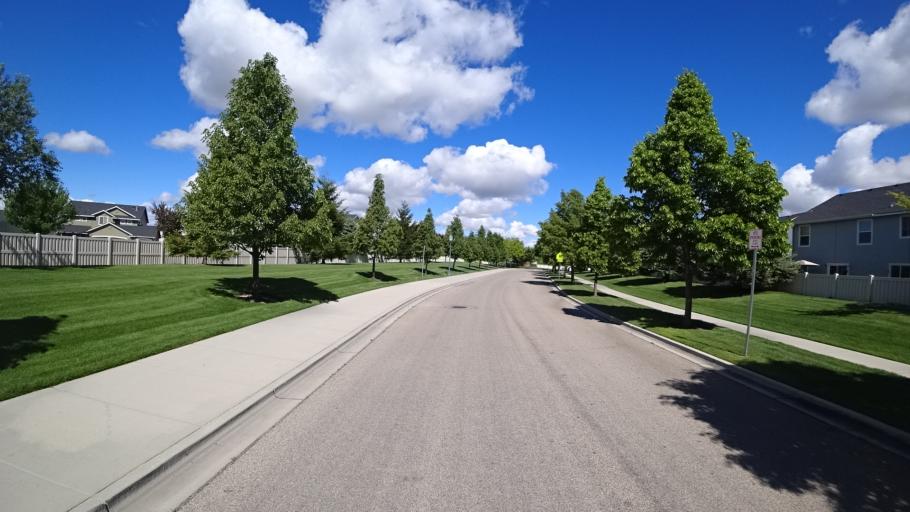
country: US
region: Idaho
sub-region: Ada County
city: Kuna
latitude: 43.5062
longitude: -116.4426
